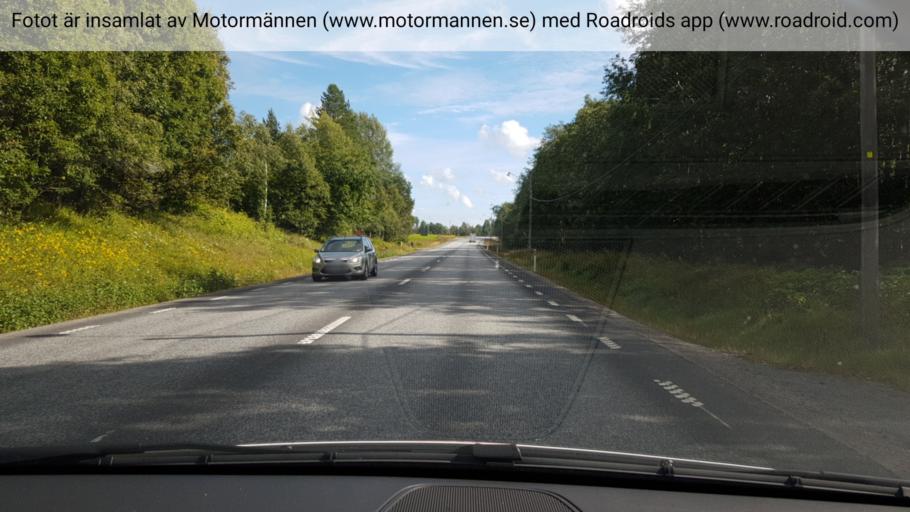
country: SE
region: Vaesterbotten
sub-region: Umea Kommun
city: Roback
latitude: 63.8806
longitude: 20.0467
